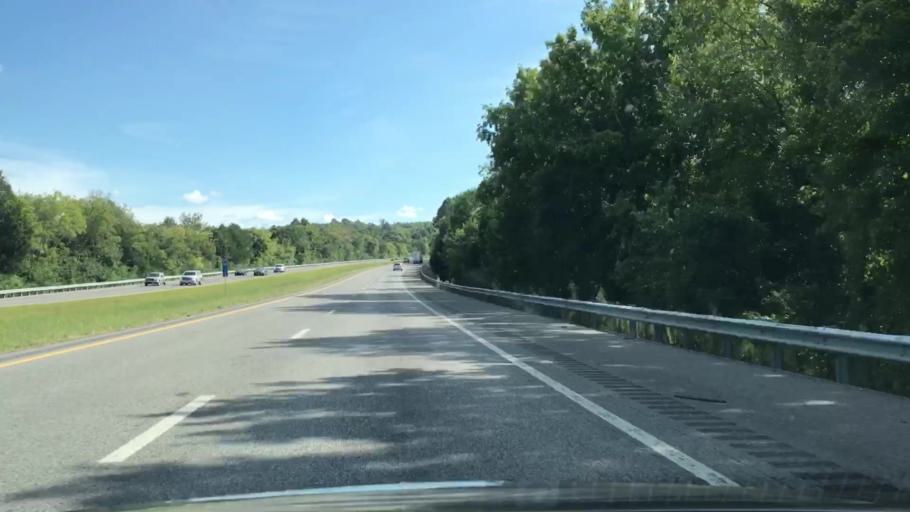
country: US
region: Alabama
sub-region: Limestone County
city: Ardmore
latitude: 35.1281
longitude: -86.8775
